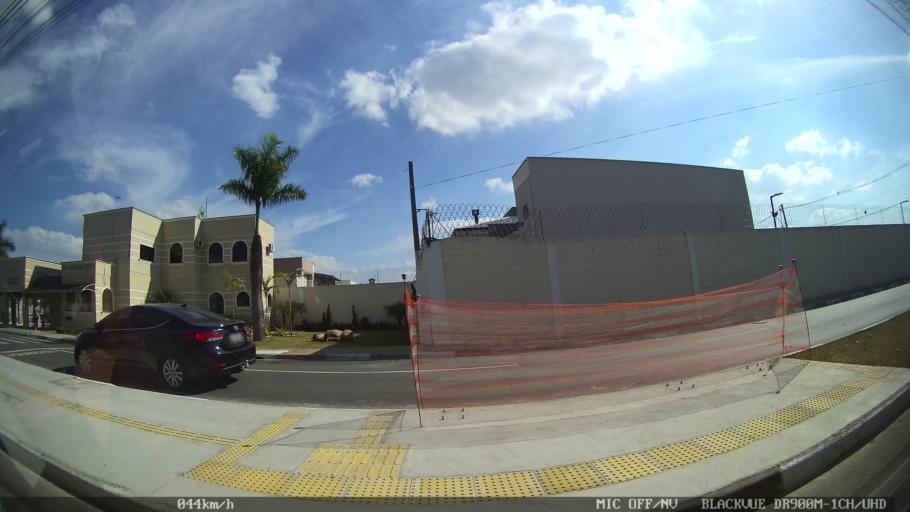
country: BR
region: Sao Paulo
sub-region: Hortolandia
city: Hortolandia
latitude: -22.8806
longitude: -47.2308
